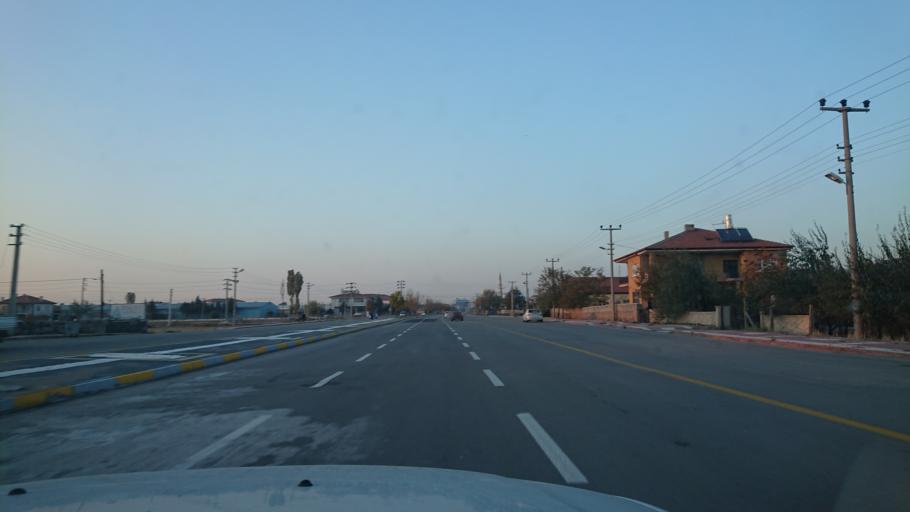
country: TR
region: Aksaray
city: Aksaray
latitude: 38.3433
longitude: 34.0459
